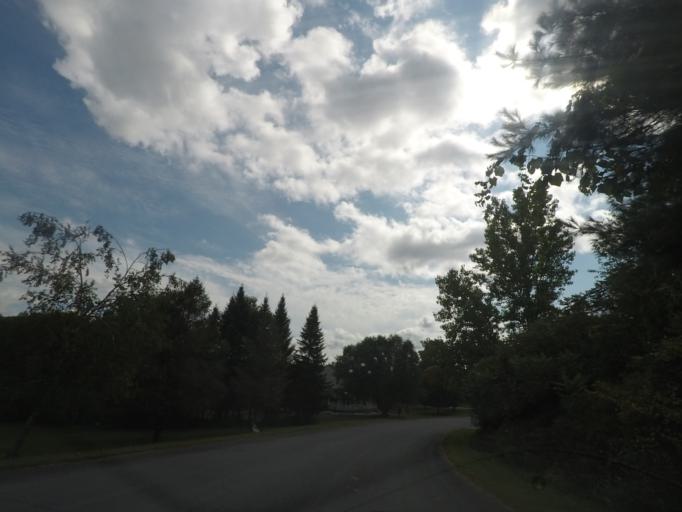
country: US
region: New York
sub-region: Rensselaer County
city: West Sand Lake
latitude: 42.5911
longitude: -73.6198
